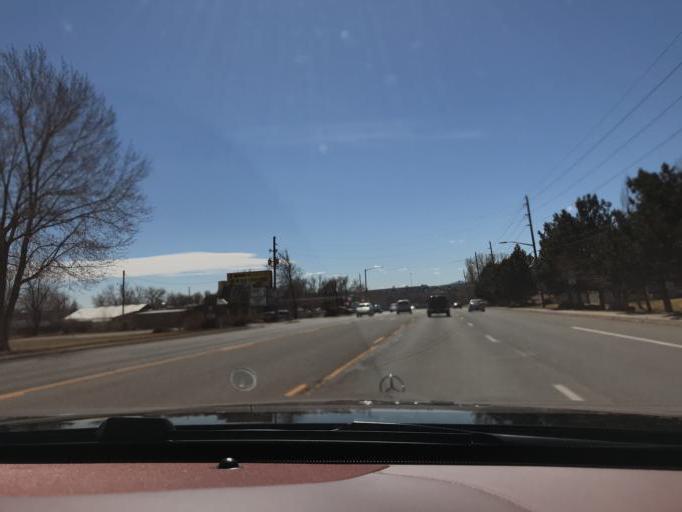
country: US
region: Colorado
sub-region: Jefferson County
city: Applewood
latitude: 39.7856
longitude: -105.1381
